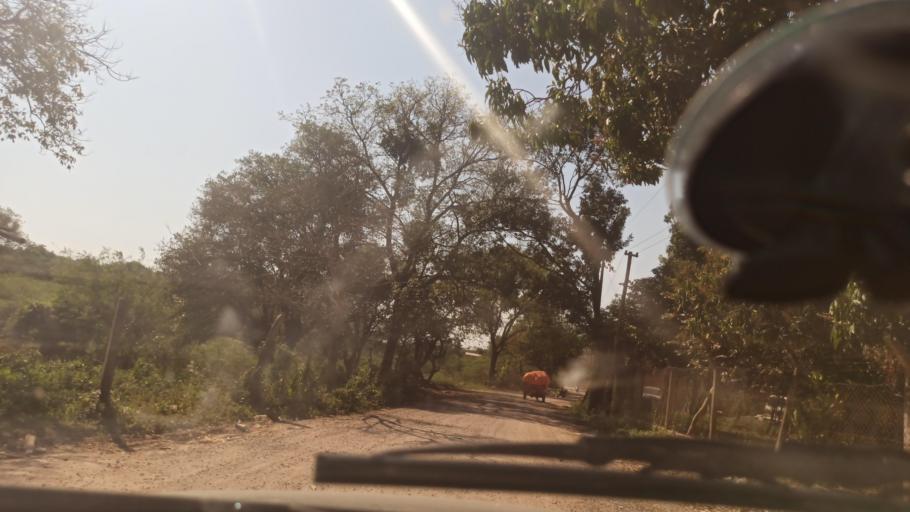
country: AR
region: Formosa
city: Clorinda
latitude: -25.2998
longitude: -57.7065
